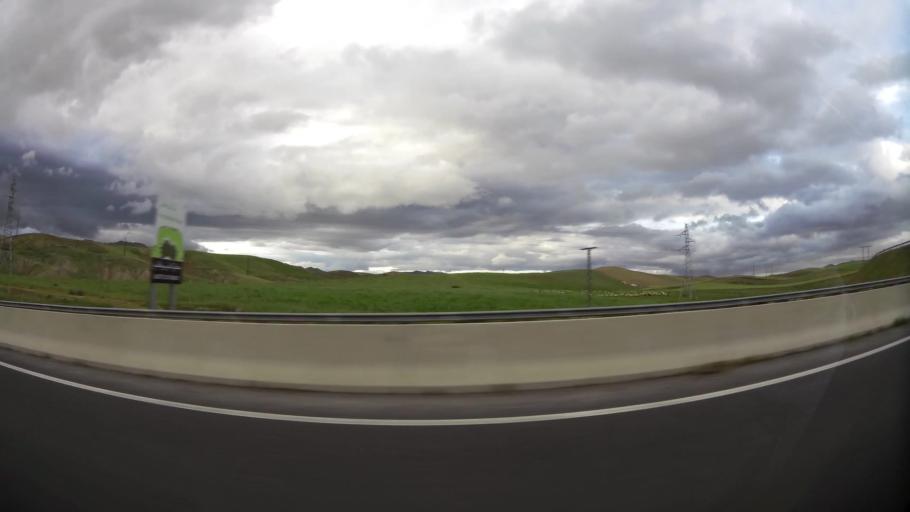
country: MA
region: Taza-Al Hoceima-Taounate
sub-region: Taza
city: Taza
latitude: 34.2574
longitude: -3.9340
